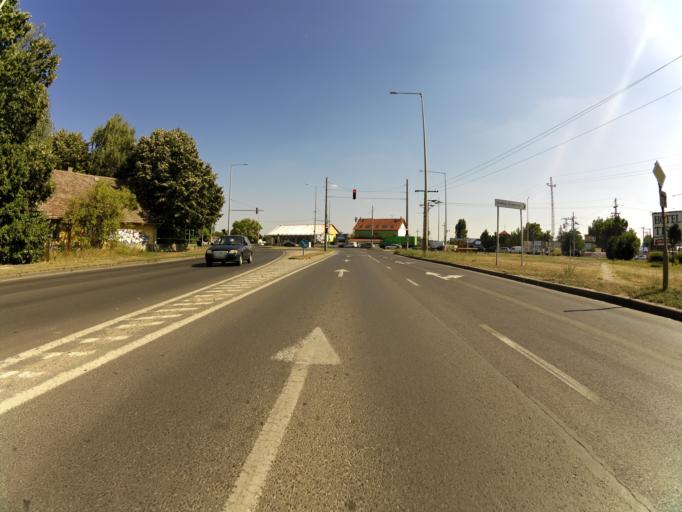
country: HU
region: Csongrad
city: Szeged
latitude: 46.2684
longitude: 20.1037
